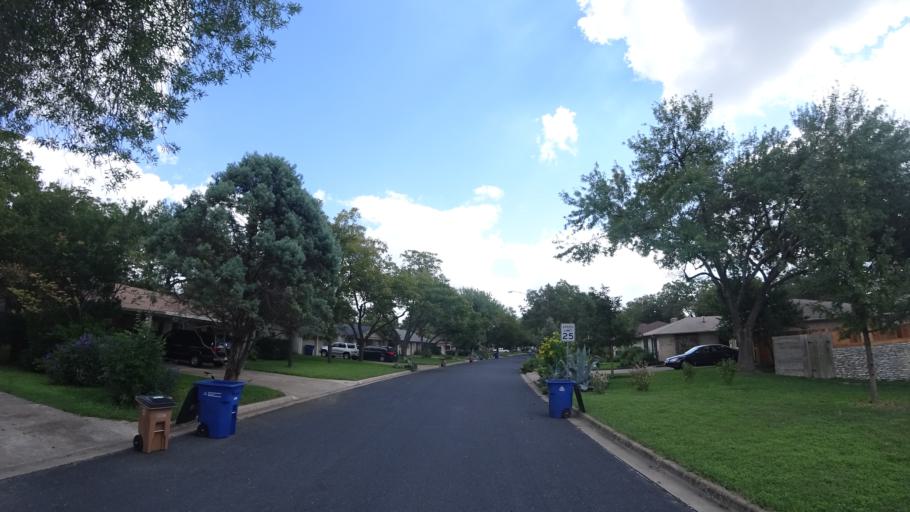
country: US
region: Texas
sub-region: Williamson County
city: Jollyville
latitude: 30.3608
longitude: -97.7279
